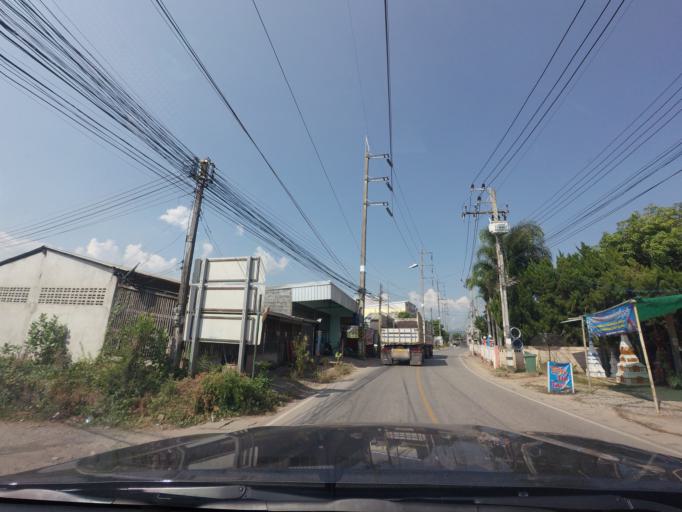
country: TH
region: Phitsanulok
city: Nakhon Thai
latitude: 17.1042
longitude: 100.8390
